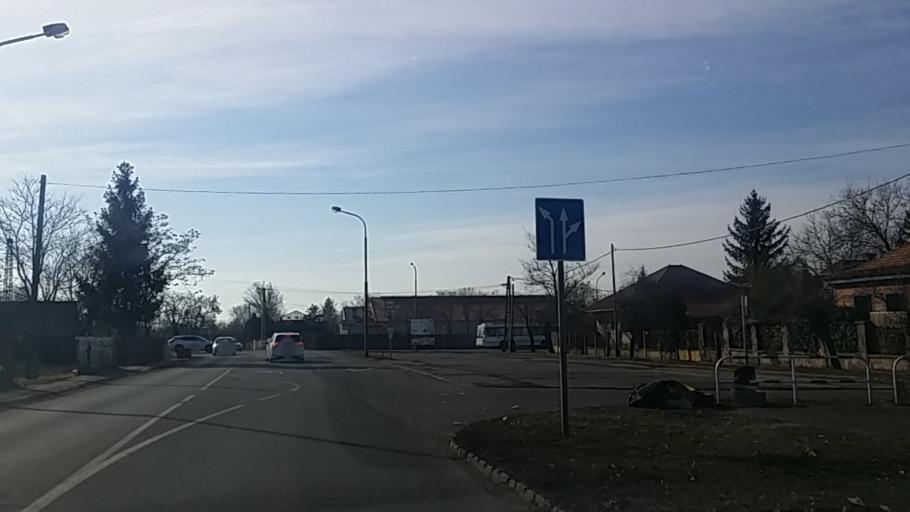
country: HU
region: Heves
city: Gyongyos
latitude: 47.7813
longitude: 19.9366
